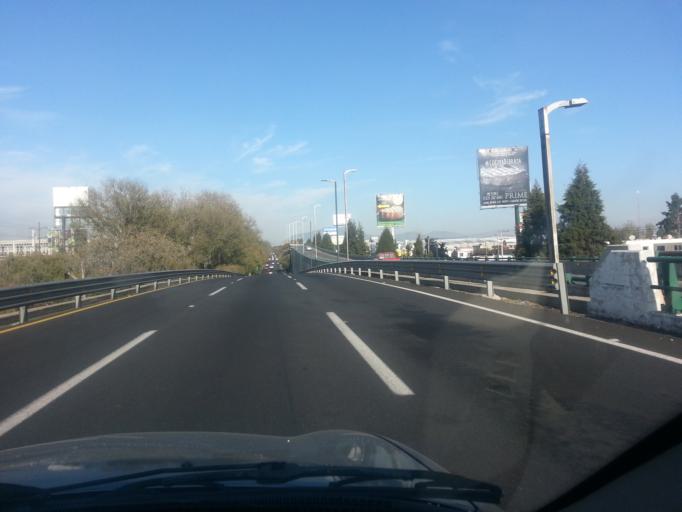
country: MX
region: Mexico
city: Santa Maria Totoltepec
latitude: 19.2869
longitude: -99.5736
